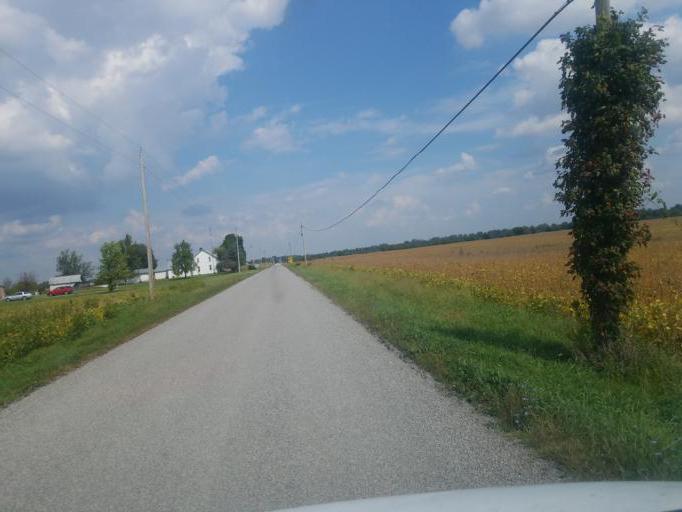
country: US
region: Ohio
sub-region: Hardin County
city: Kenton
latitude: 40.6438
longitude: -83.6819
